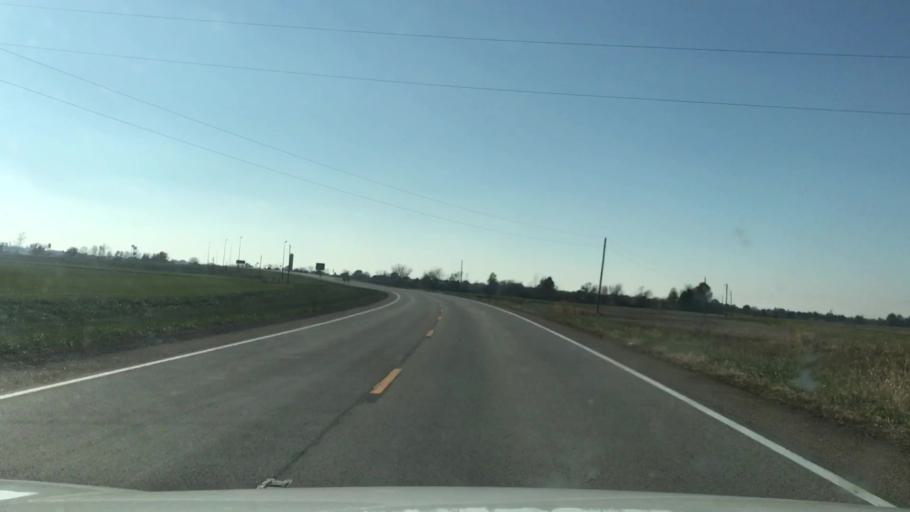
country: US
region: Illinois
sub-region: Washington County
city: Okawville
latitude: 38.4427
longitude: -89.5232
